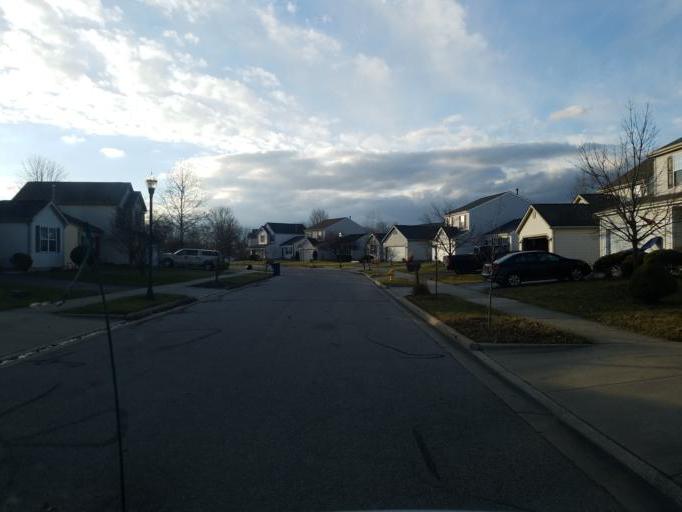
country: US
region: Ohio
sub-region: Delaware County
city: Delaware
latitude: 40.3176
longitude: -83.1133
